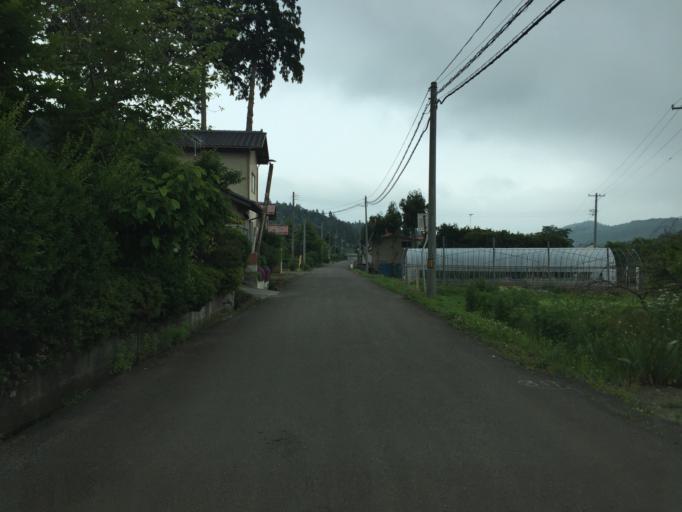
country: JP
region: Fukushima
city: Yanagawamachi-saiwaicho
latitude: 37.7681
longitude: 140.7124
